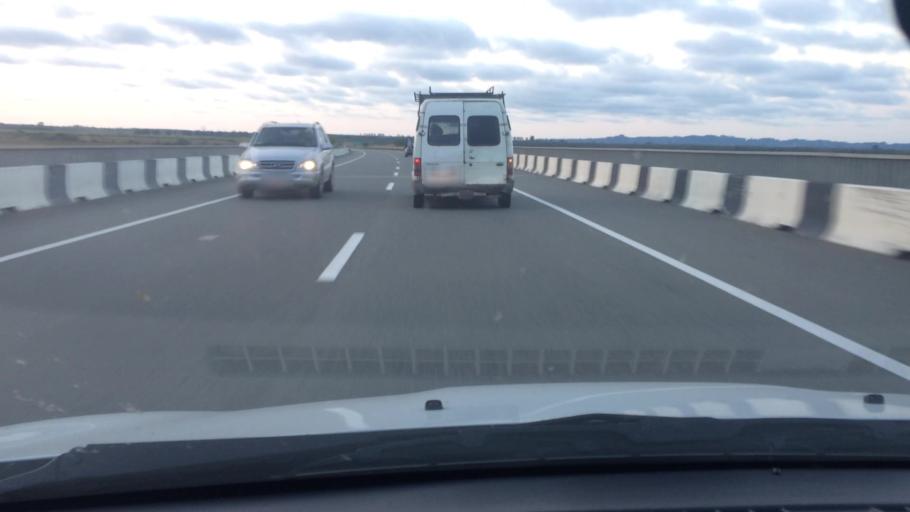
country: GE
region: Ajaria
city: Ochkhamuri
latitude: 41.8670
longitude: 41.8352
